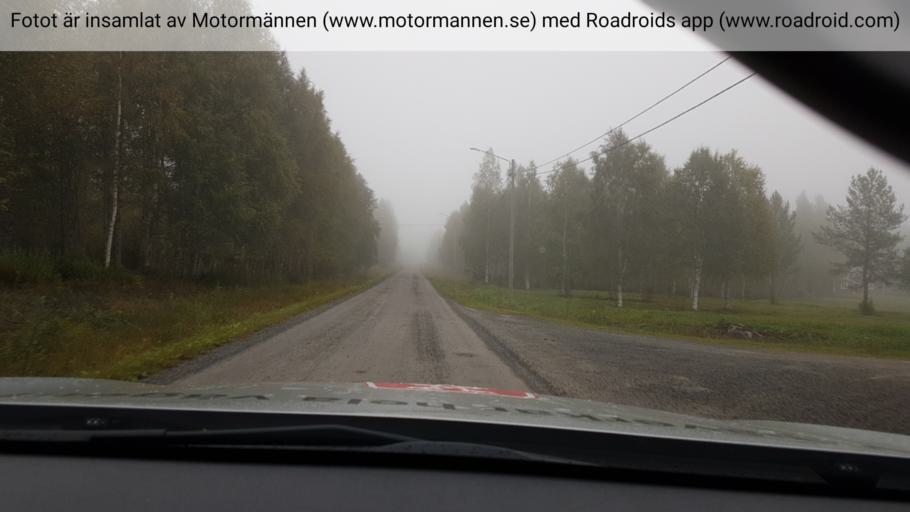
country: SE
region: Vaesterbotten
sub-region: Umea Kommun
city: Ersmark
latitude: 64.1173
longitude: 20.3659
